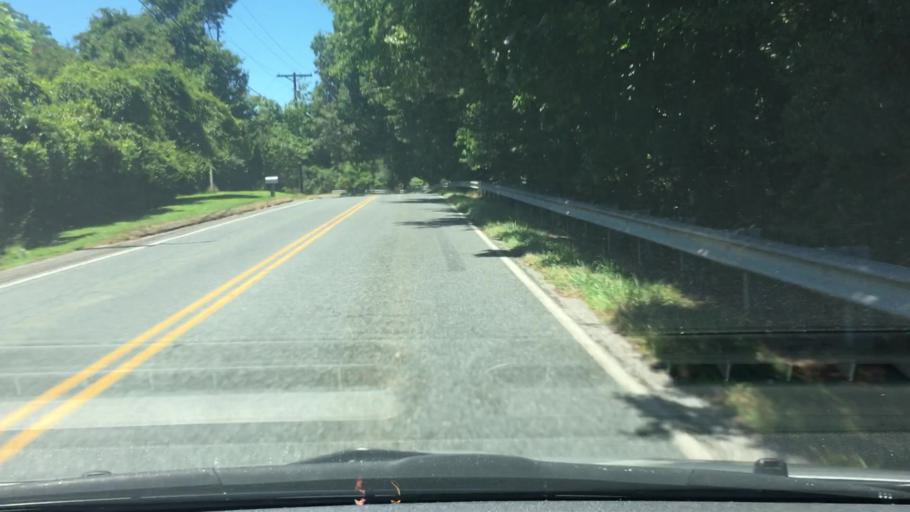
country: US
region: Maryland
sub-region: Saint Mary's County
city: Leonardtown
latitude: 38.3690
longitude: -76.5874
